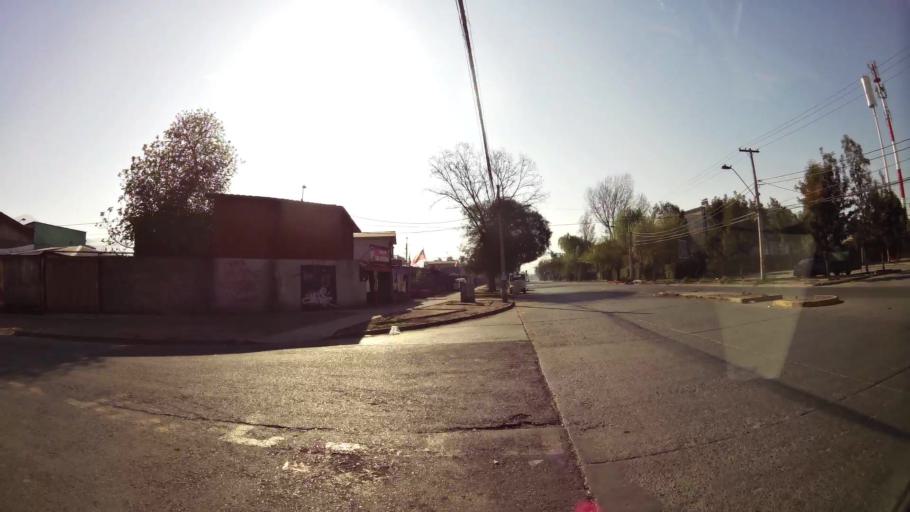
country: CL
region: Santiago Metropolitan
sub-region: Provincia de Santiago
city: Santiago
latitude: -33.3863
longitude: -70.6669
